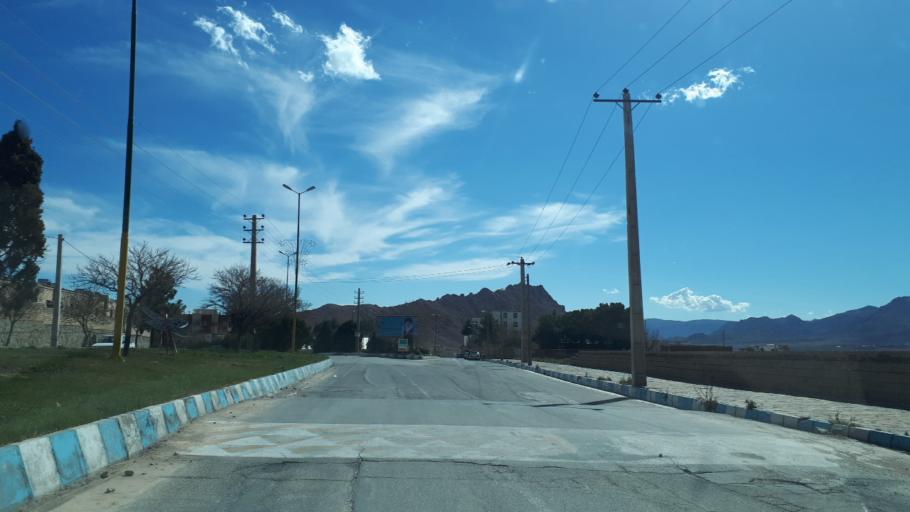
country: IR
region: Semnan
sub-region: Mahdishahr
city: Mahdishahr
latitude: 35.6983
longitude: 53.3449
